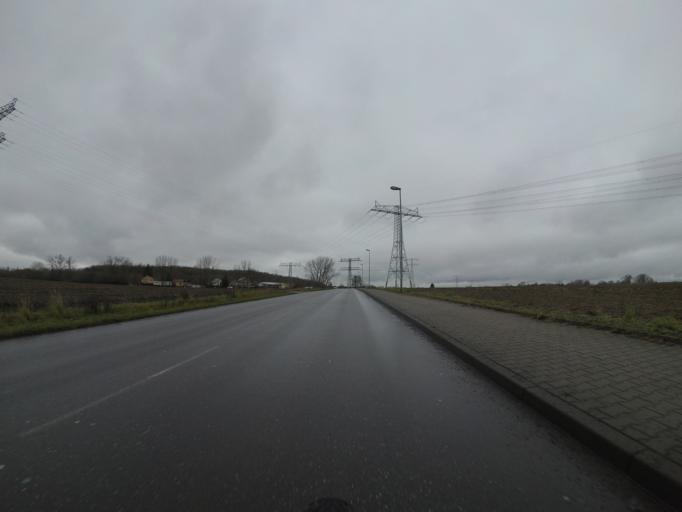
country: DE
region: Berlin
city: Hellersdorf
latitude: 52.5529
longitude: 13.5938
